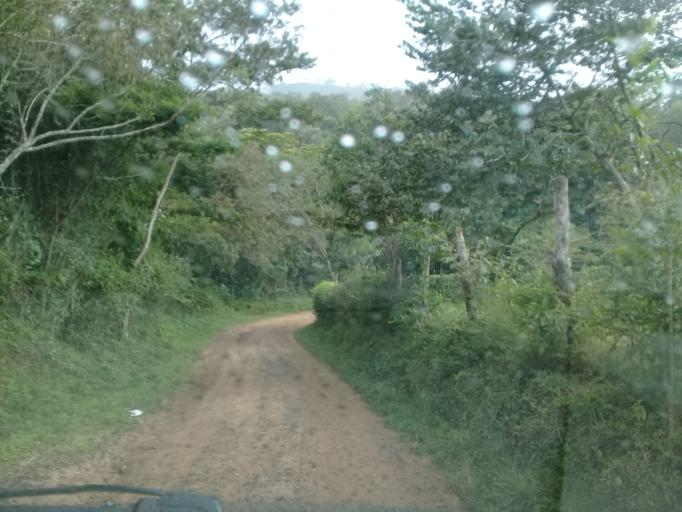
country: CO
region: Cundinamarca
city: Guaduas
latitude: 5.1161
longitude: -74.6094
